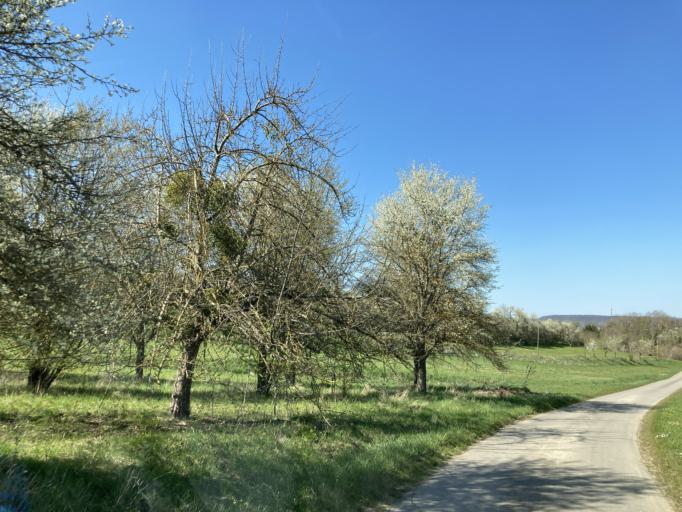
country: DE
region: Baden-Wuerttemberg
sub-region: Tuebingen Region
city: Rottenburg
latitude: 48.5359
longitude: 8.9120
